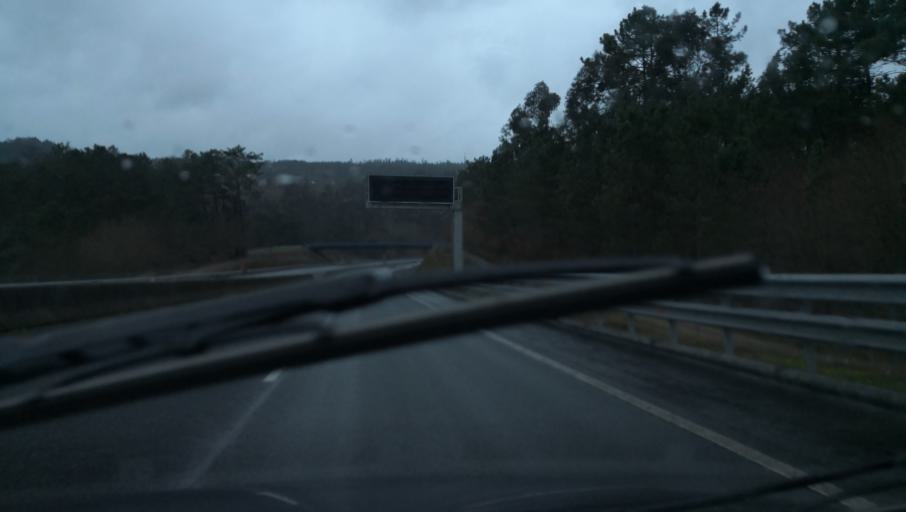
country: ES
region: Galicia
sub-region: Provincia da Coruna
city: Santiago de Compostela
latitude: 42.8268
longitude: -8.5196
